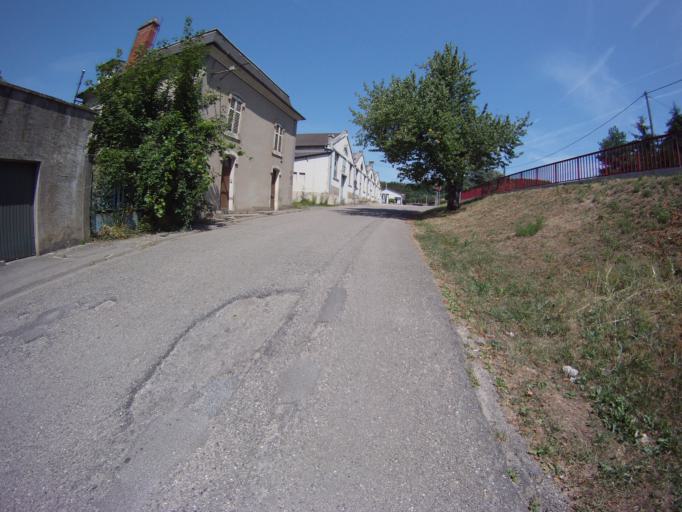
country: FR
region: Lorraine
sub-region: Departement de Meurthe-et-Moselle
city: Liverdun
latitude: 48.7466
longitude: 6.0663
